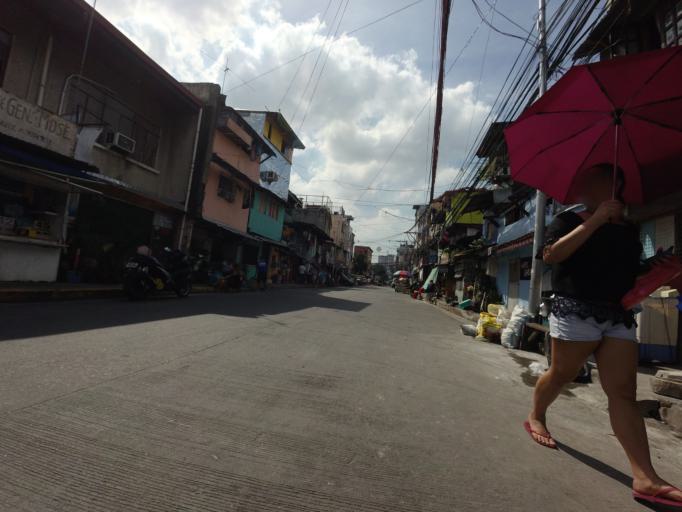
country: PH
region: Metro Manila
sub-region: Makati City
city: Makati City
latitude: 14.5721
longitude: 121.0067
